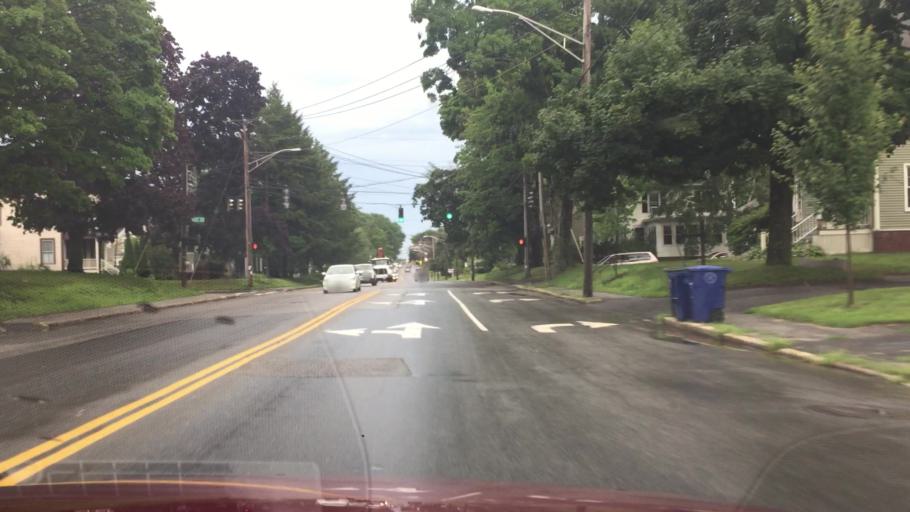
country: US
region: Maine
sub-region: Cumberland County
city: Westbrook
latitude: 43.6809
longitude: -70.3458
